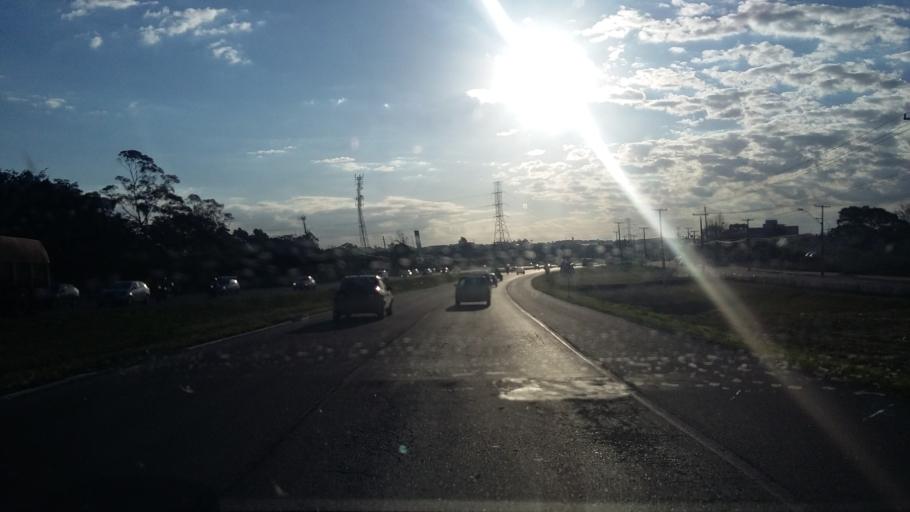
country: BR
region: Parana
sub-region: Araucaria
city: Araucaria
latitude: -25.5312
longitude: -49.3237
